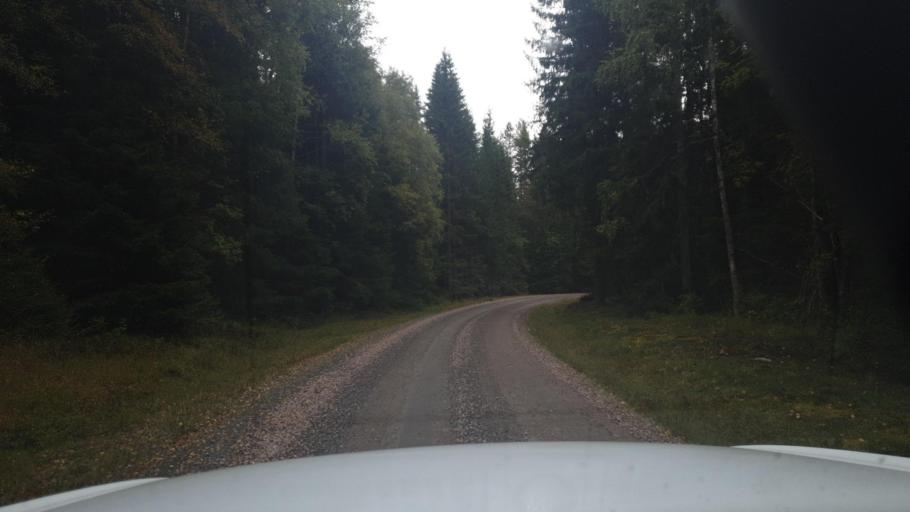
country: SE
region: Vaermland
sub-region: Eda Kommun
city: Charlottenberg
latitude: 60.1443
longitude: 12.5986
